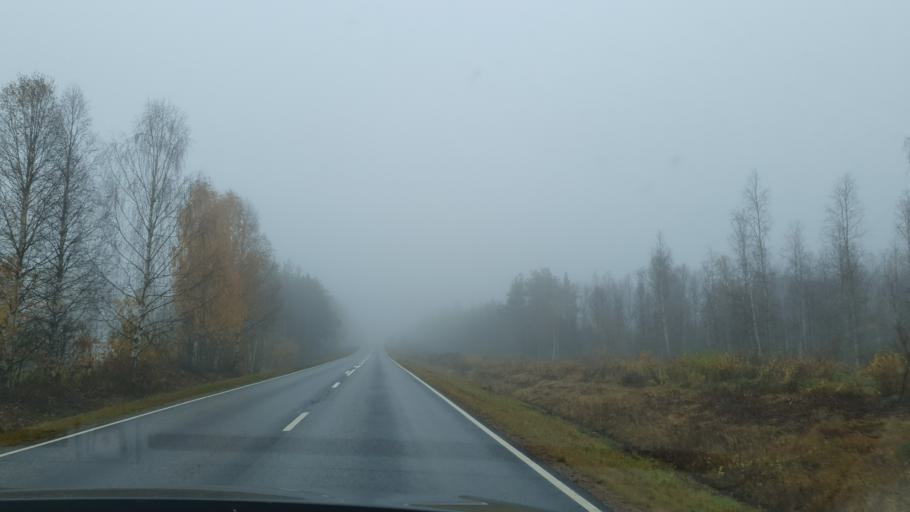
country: FI
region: Lapland
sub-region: Rovaniemi
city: Rovaniemi
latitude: 66.7939
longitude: 25.4153
